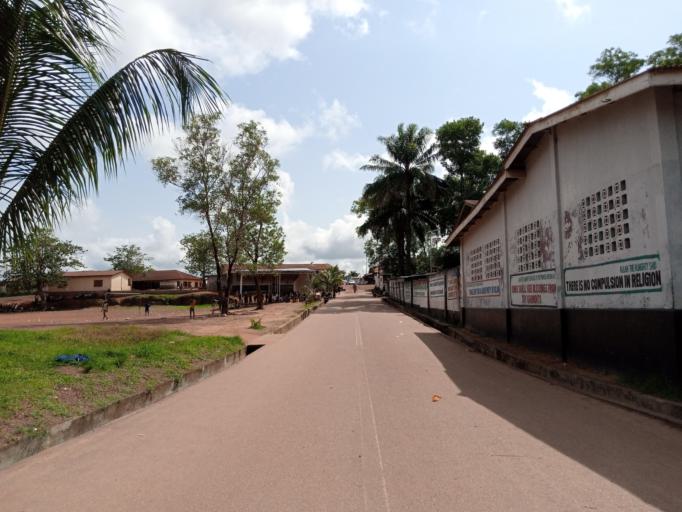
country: SL
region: Southern Province
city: Bo
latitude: 7.9708
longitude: -11.7349
